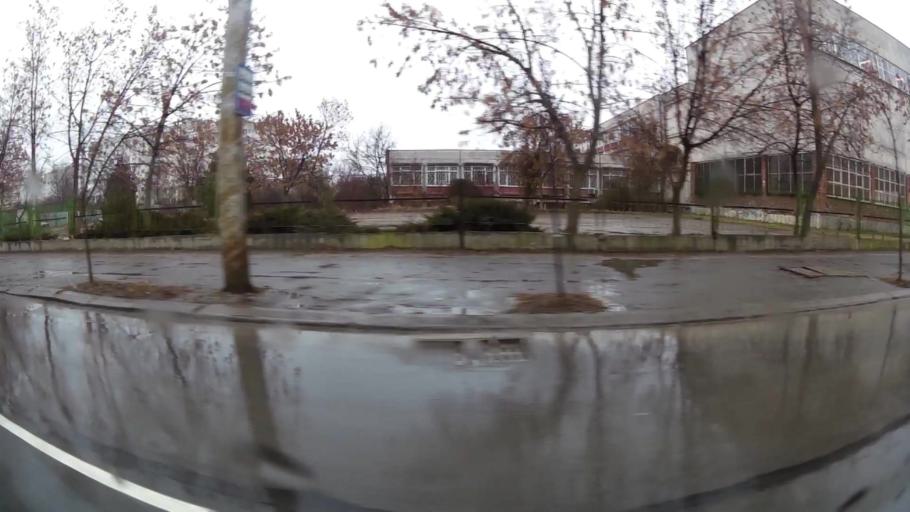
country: BG
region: Sofia-Capital
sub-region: Stolichna Obshtina
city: Sofia
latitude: 42.6451
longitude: 23.4049
